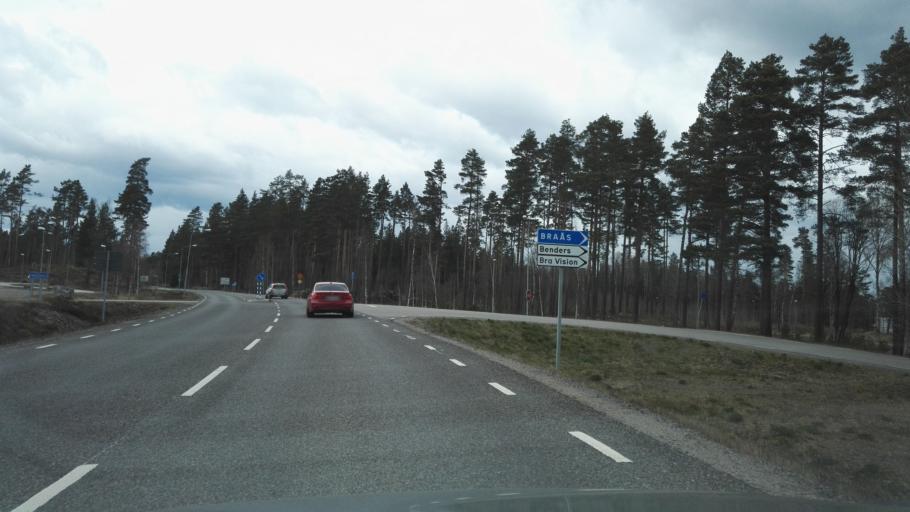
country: SE
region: Kronoberg
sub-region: Vaxjo Kommun
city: Braas
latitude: 57.0585
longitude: 15.0376
